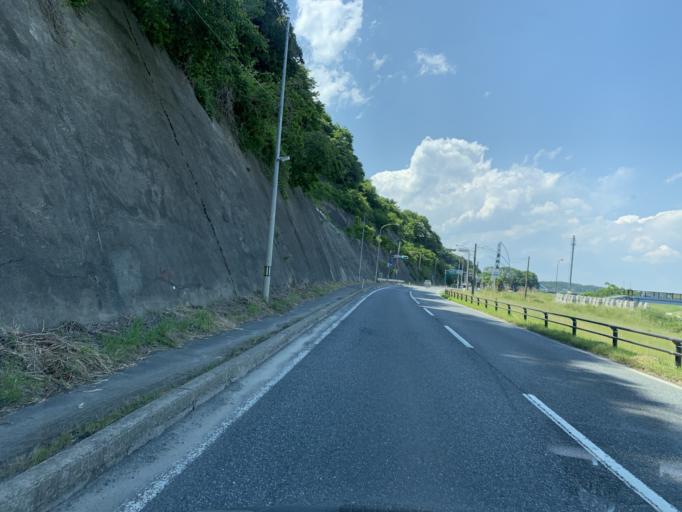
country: JP
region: Miyagi
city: Yamoto
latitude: 38.4054
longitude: 141.1475
